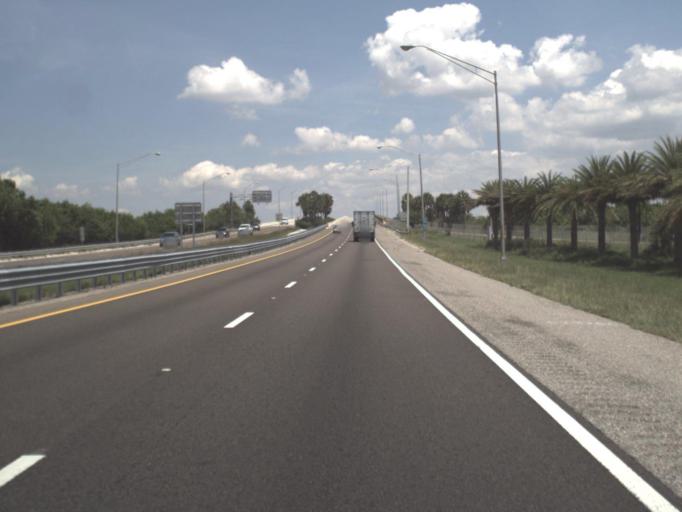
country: US
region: Florida
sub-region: Pinellas County
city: Tierra Verde
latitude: 27.6863
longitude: -82.6784
